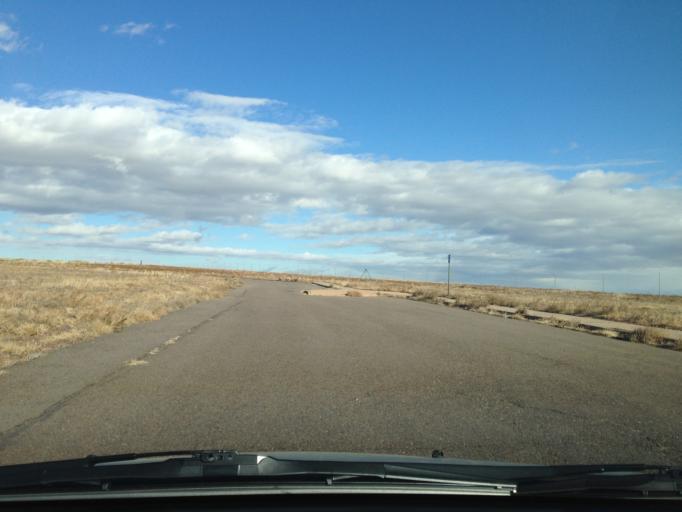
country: US
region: Colorado
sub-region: Adams County
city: Derby
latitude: 39.8319
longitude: -104.8555
